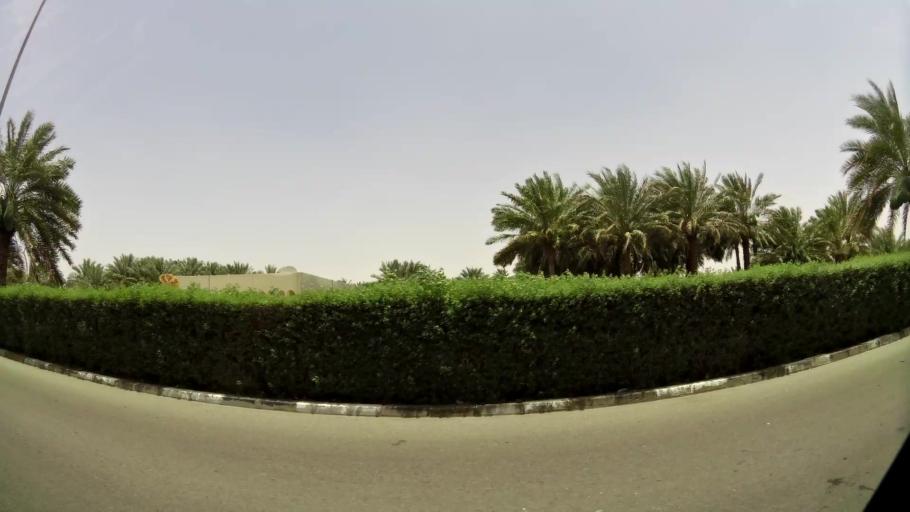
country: AE
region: Abu Dhabi
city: Al Ain
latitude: 24.2168
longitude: 55.7353
